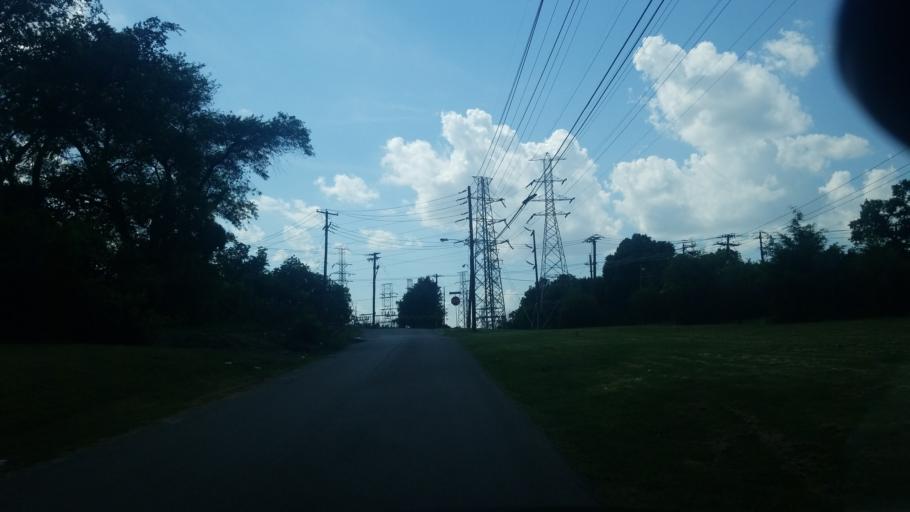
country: US
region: Texas
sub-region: Dallas County
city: Dallas
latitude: 32.7212
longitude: -96.7997
